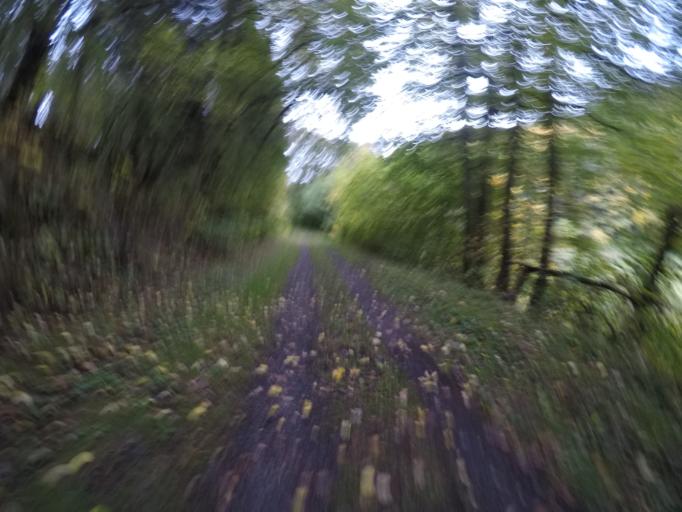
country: BE
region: Wallonia
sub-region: Province du Luxembourg
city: Fauvillers
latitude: 49.8580
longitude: 5.6962
